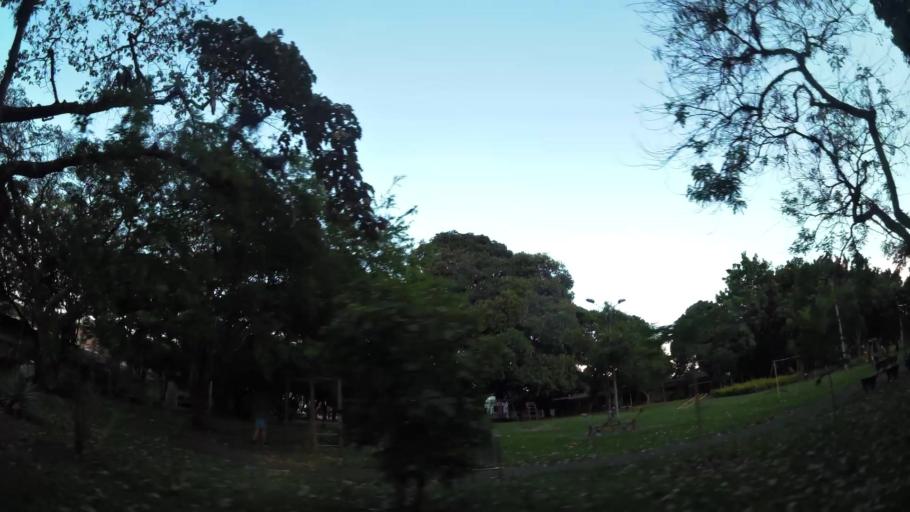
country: CO
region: Valle del Cauca
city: Cali
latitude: 3.4083
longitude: -76.5519
